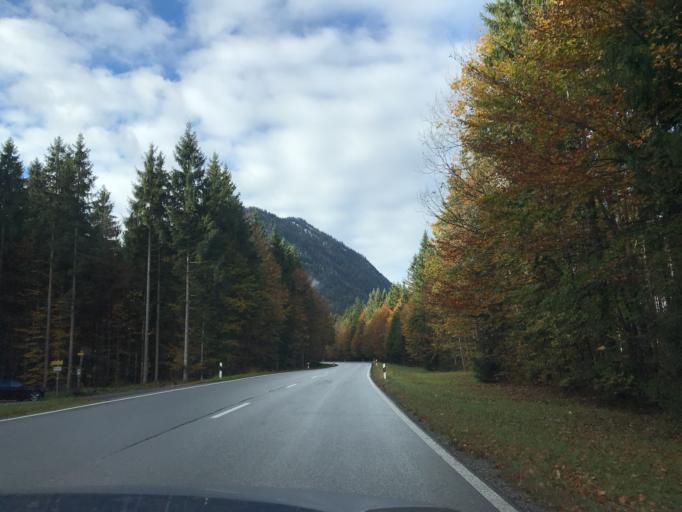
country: DE
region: Bavaria
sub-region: Upper Bavaria
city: Jachenau
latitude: 47.5656
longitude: 11.5221
